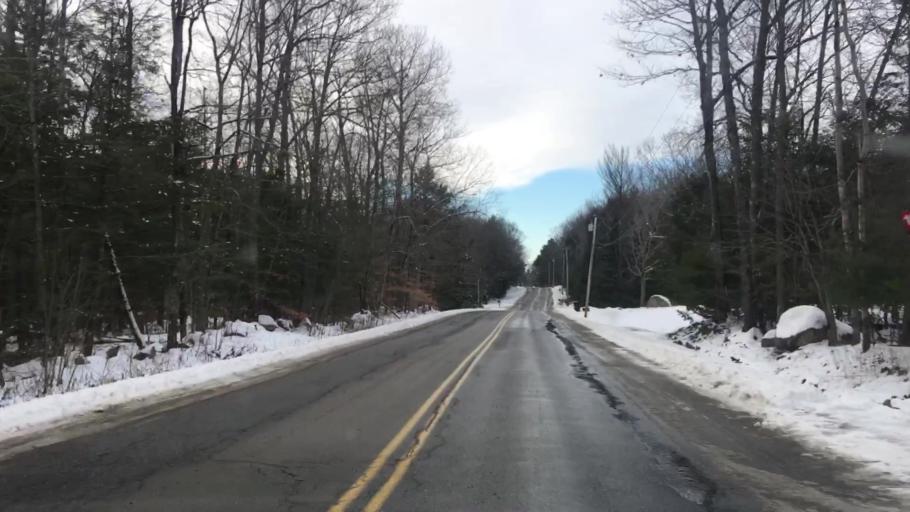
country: US
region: Maine
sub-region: Kennebec County
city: Chelsea
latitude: 44.2539
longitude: -69.7380
